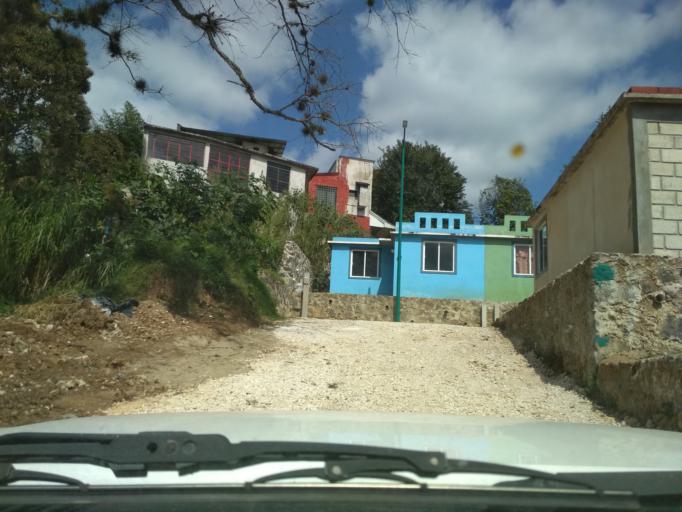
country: MX
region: Veracruz
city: Coatepec
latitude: 19.4521
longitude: -96.9514
